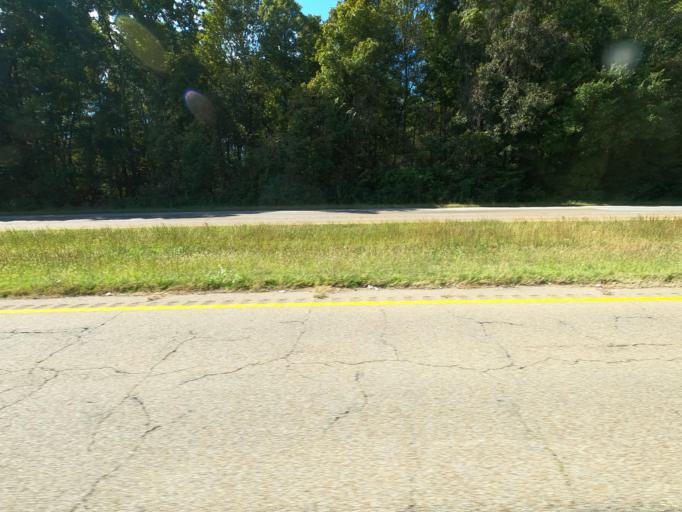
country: US
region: Tennessee
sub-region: Crockett County
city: Alamo
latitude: 35.7562
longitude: -89.1128
